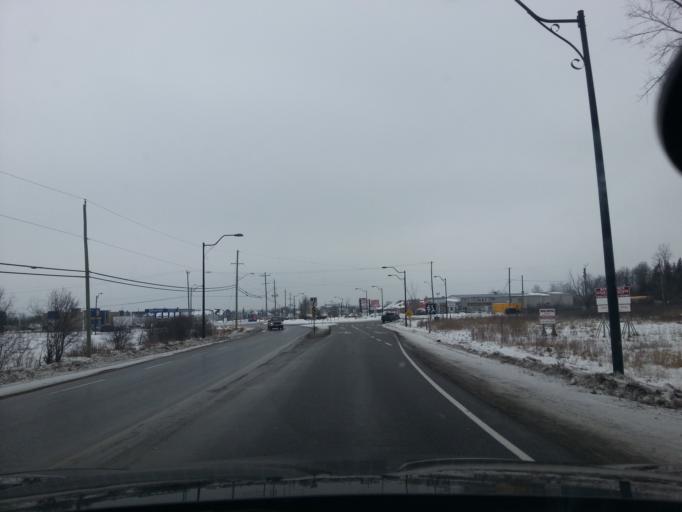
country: CA
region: Ontario
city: Carleton Place
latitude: 45.2380
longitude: -76.1779
